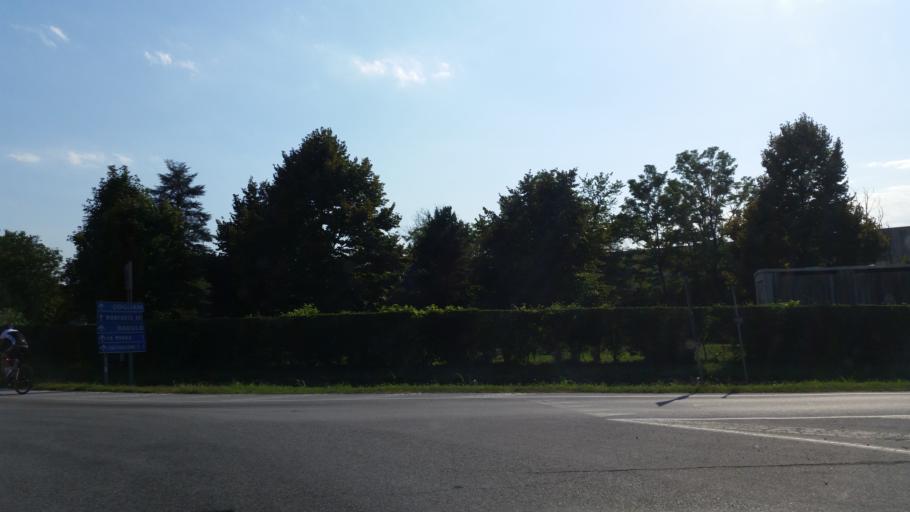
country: IT
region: Piedmont
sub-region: Provincia di Cuneo
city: Grinzane Cavour
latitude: 44.6468
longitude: 7.9779
